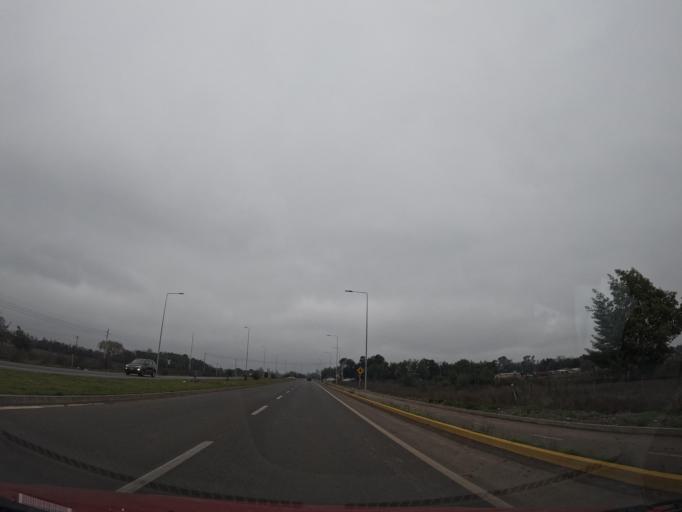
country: CL
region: Maule
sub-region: Provincia de Talca
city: San Clemente
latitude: -35.5267
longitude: -71.4804
